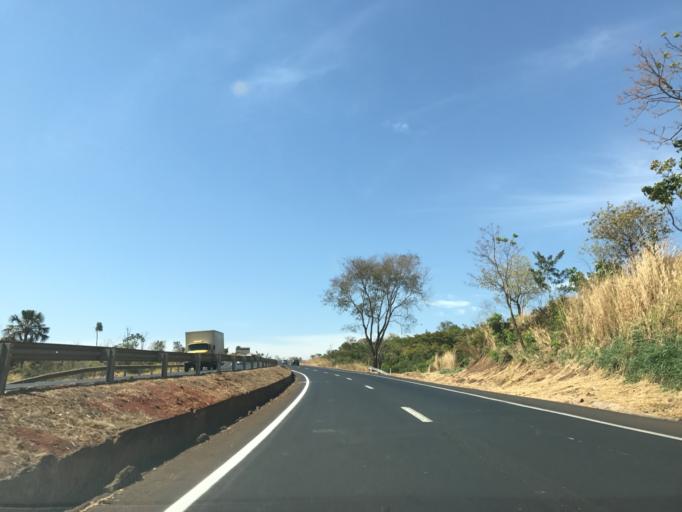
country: BR
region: Minas Gerais
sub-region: Monte Alegre De Minas
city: Monte Alegre de Minas
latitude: -18.7942
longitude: -49.0841
